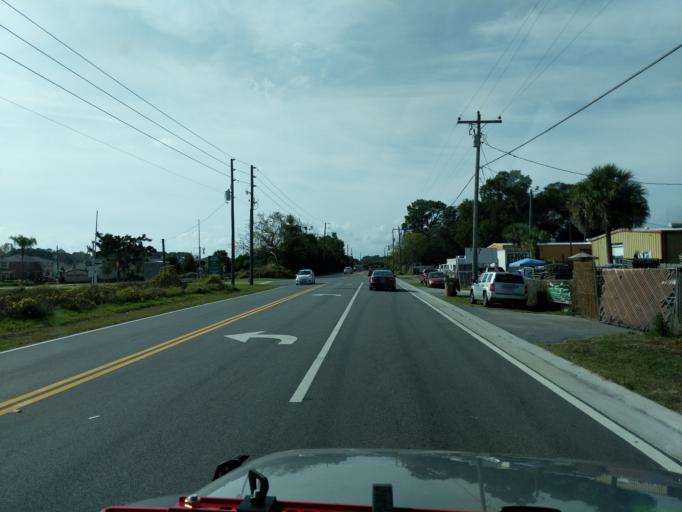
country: US
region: Florida
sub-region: Lake County
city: Tavares
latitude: 28.8032
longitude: -81.6990
